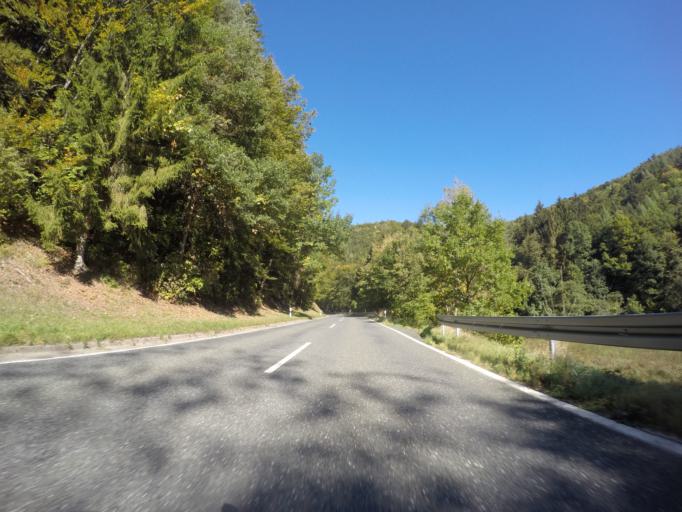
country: DE
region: Bavaria
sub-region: Upper Franconia
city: Gossweinstein
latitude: 49.7976
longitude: 11.3317
